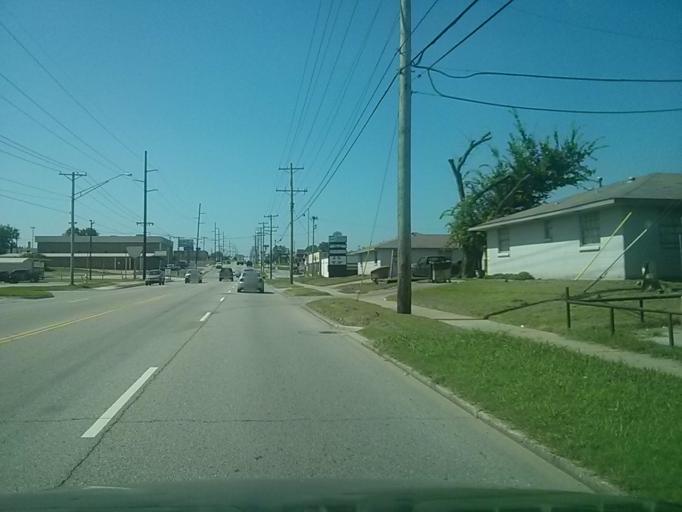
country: US
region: Oklahoma
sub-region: Tulsa County
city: Tulsa
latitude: 36.1520
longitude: -95.9046
